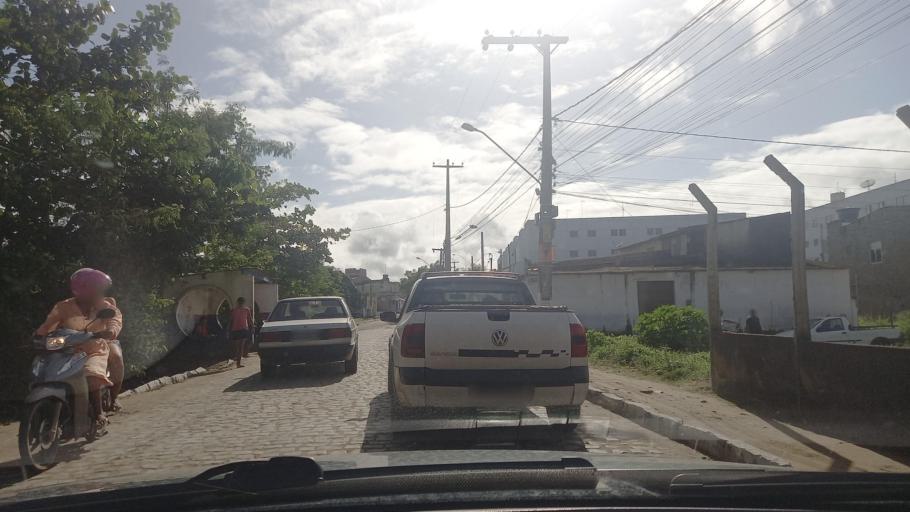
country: BR
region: Pernambuco
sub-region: Vitoria De Santo Antao
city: Vitoria de Santo Antao
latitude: -8.0984
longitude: -35.2786
